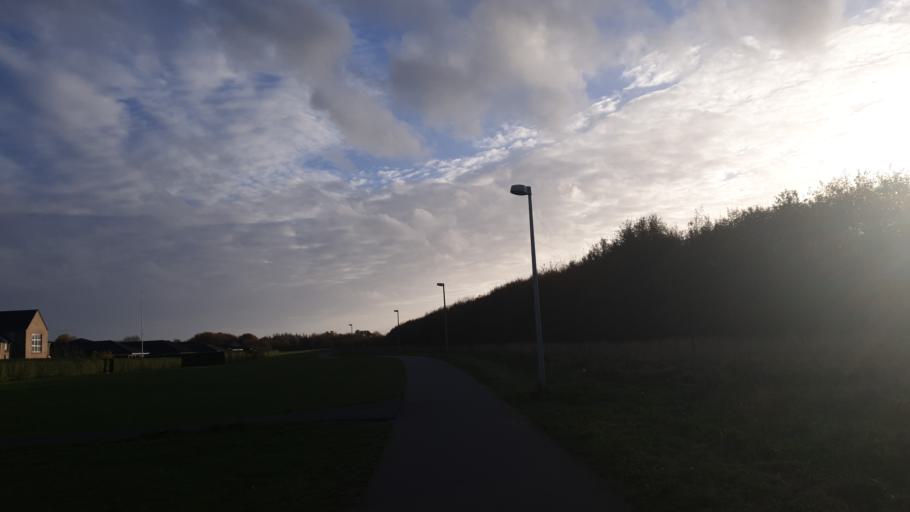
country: DK
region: Central Jutland
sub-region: Hedensted Kommune
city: Hedensted
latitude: 55.7874
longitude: 9.6919
